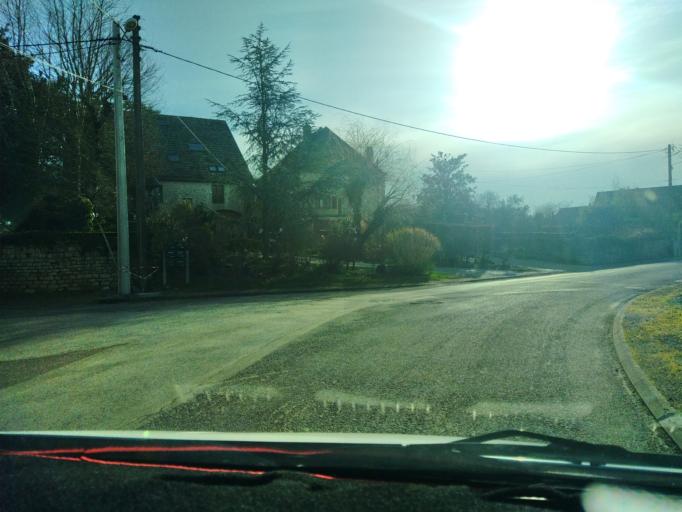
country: FR
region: Franche-Comte
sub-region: Departement de la Haute-Saone
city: Marnay
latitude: 47.3219
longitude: 5.6842
